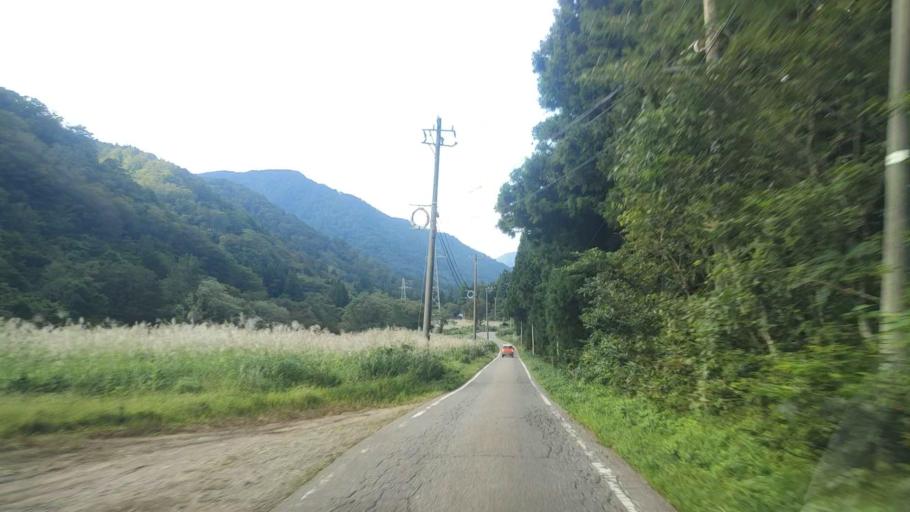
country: JP
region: Toyama
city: Yatsuomachi-higashikumisaka
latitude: 36.4438
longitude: 137.0842
